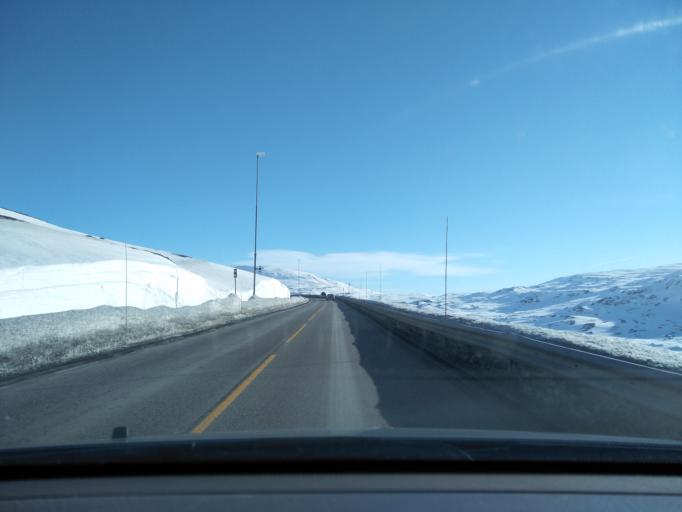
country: NO
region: Aust-Agder
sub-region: Bykle
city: Hovden
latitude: 59.8439
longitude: 6.9738
